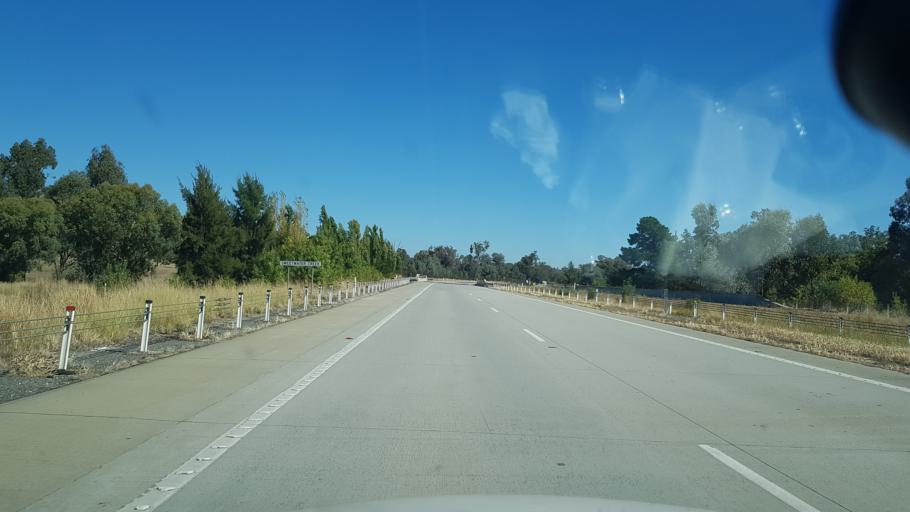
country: AU
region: New South Wales
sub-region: Greater Hume Shire
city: Holbrook
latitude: -35.8999
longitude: 147.1658
